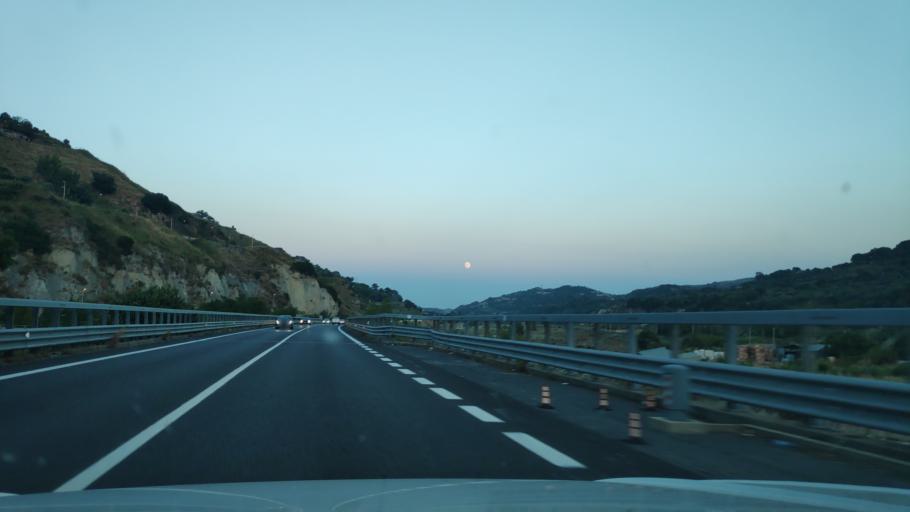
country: IT
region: Calabria
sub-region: Provincia di Reggio Calabria
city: Mammola
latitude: 38.3567
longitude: 16.2378
